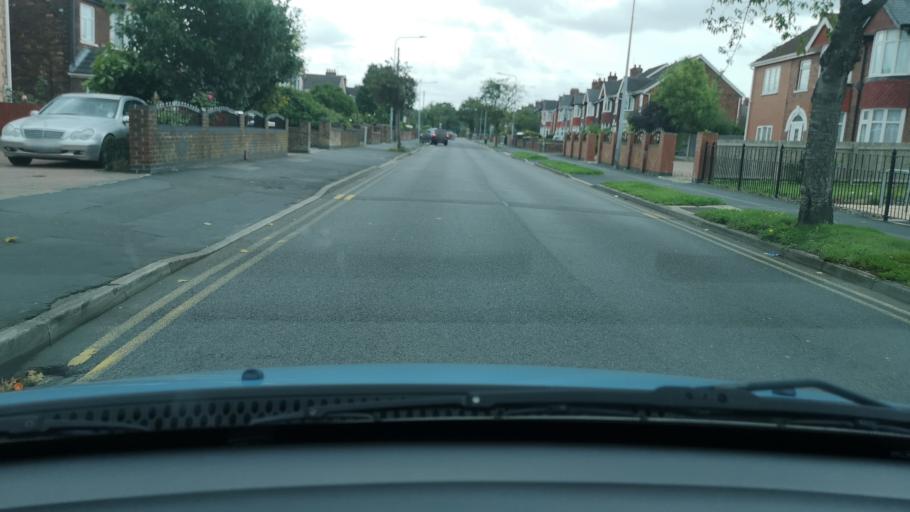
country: GB
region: England
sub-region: North Lincolnshire
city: Scunthorpe
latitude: 53.5902
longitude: -0.6610
